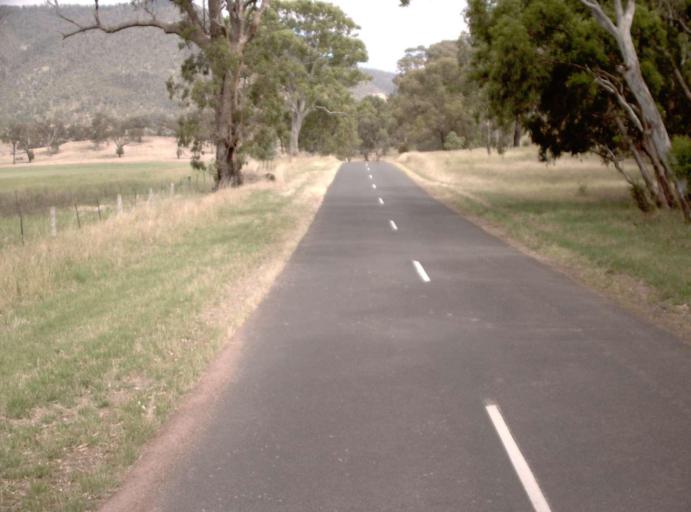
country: AU
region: Victoria
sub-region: Wellington
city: Heyfield
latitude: -37.6364
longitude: 146.6302
